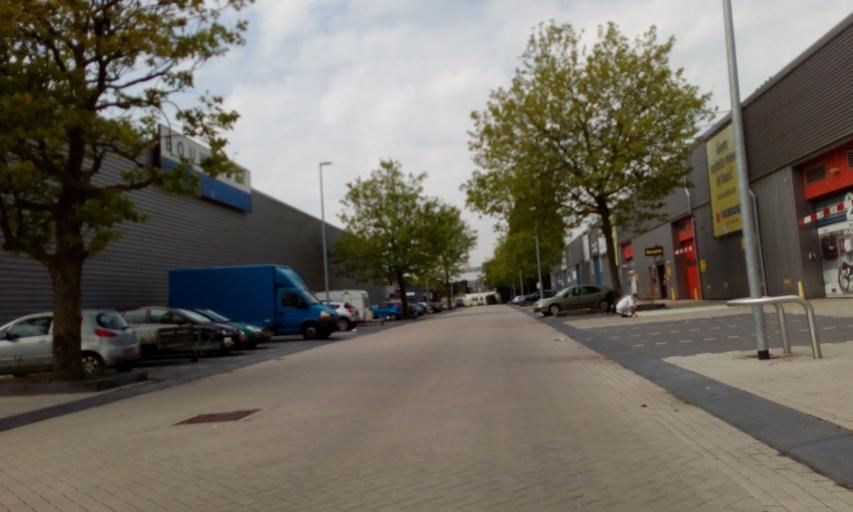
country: NL
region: South Holland
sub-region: Gemeente Schiedam
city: Schiedam
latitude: 51.9267
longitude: 4.4120
